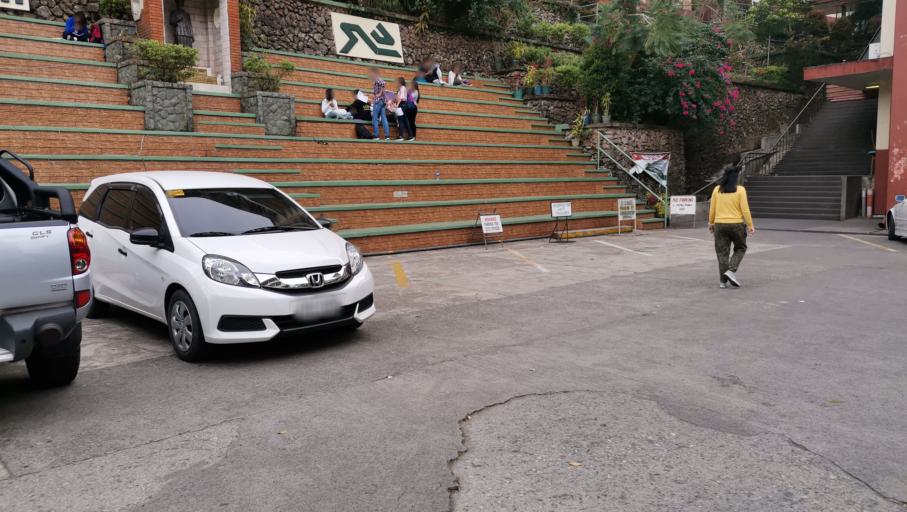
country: PH
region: Cordillera
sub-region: Baguio City
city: Baguio
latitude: 16.4183
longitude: 120.5973
